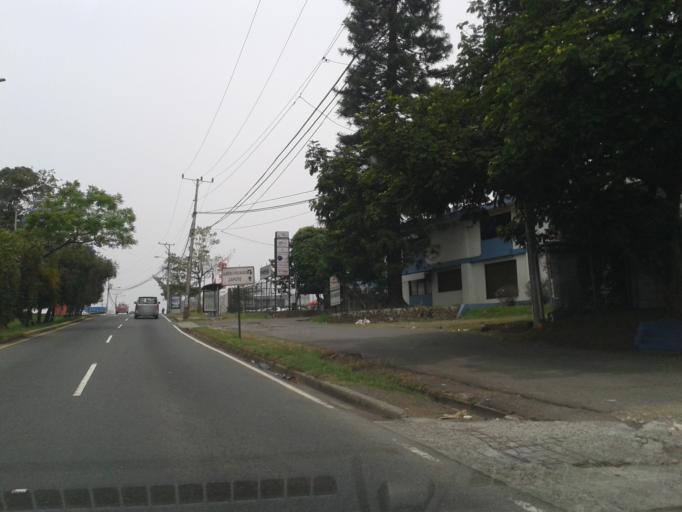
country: CR
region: San Jose
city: San Jose
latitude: 9.9240
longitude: -84.0696
